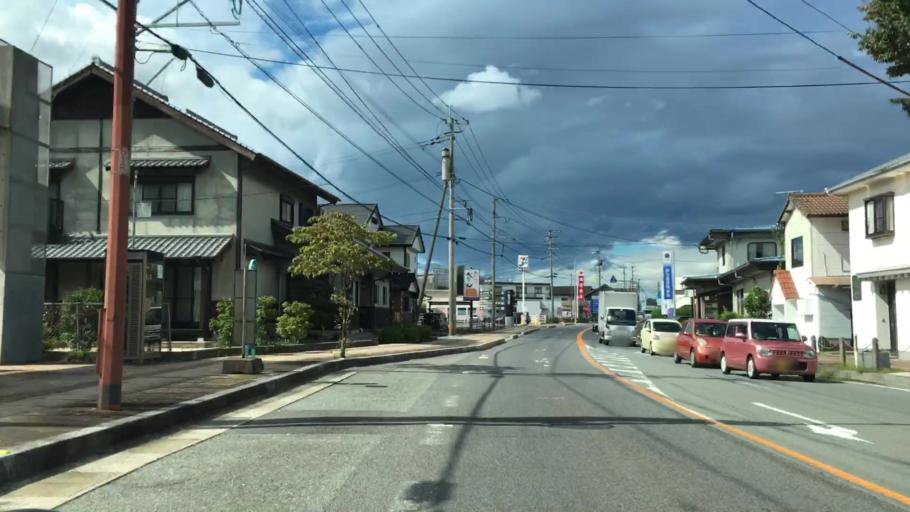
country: JP
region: Saga Prefecture
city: Imaricho-ko
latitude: 33.2108
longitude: 129.8497
